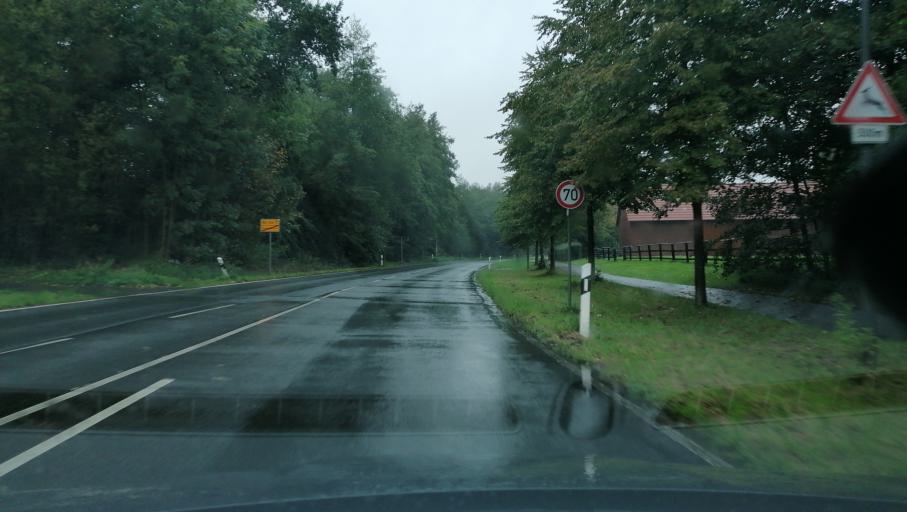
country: DE
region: North Rhine-Westphalia
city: Oer-Erkenschwick
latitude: 51.5906
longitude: 7.2573
